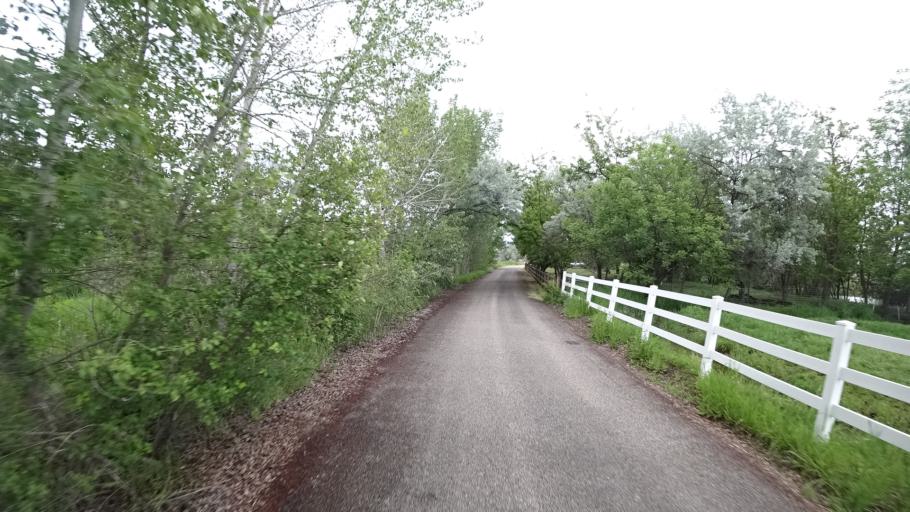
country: US
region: Idaho
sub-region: Ada County
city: Eagle
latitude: 43.6842
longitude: -116.3749
